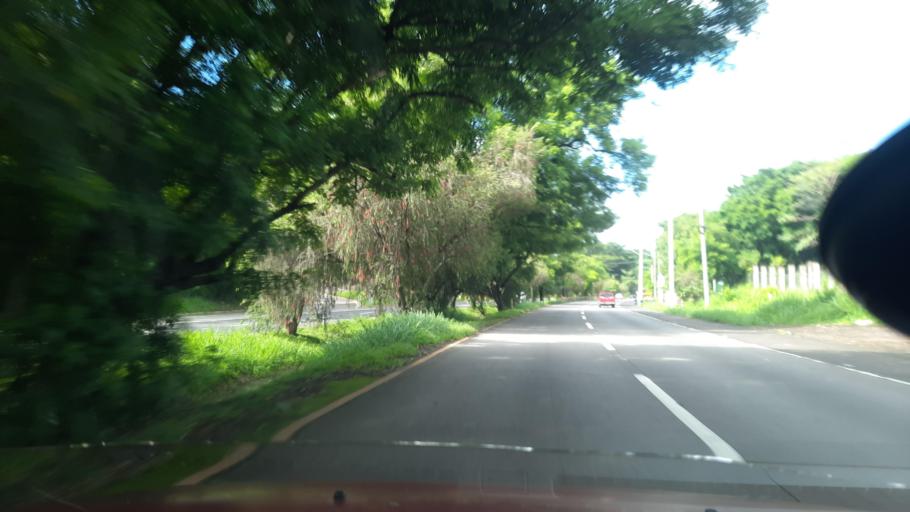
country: SV
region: La Paz
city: Olocuilta
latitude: 13.5389
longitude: -89.1110
